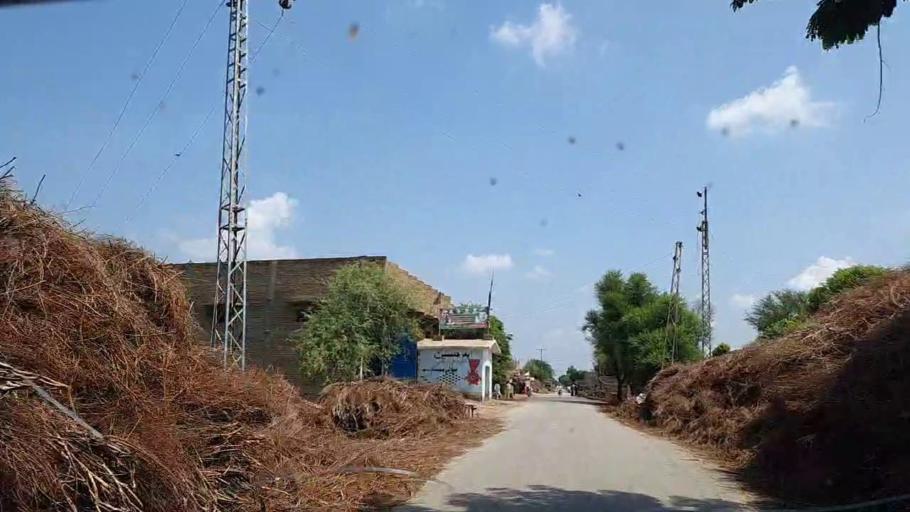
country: PK
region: Sindh
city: Tharu Shah
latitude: 26.9641
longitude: 68.0970
